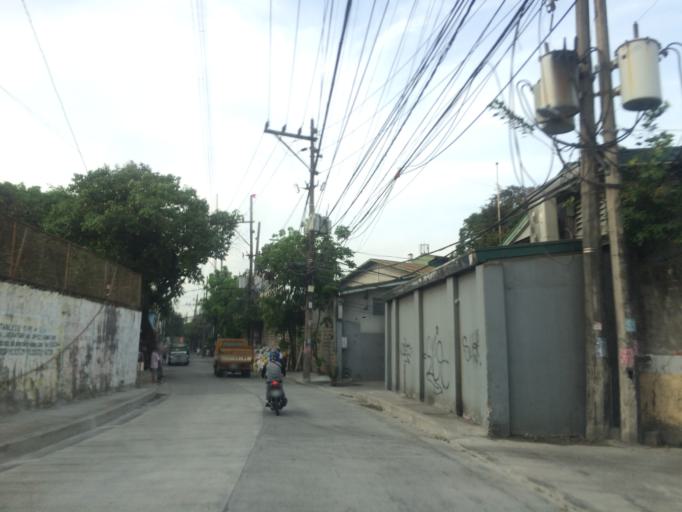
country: PH
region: Calabarzon
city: Del Monte
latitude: 14.6510
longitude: 121.0097
